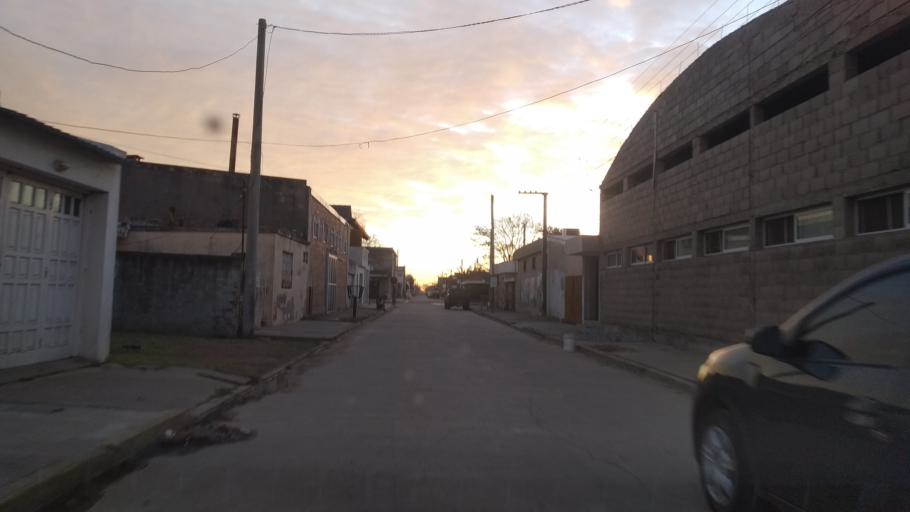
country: AR
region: Cordoba
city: Leones
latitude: -32.6297
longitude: -62.4789
